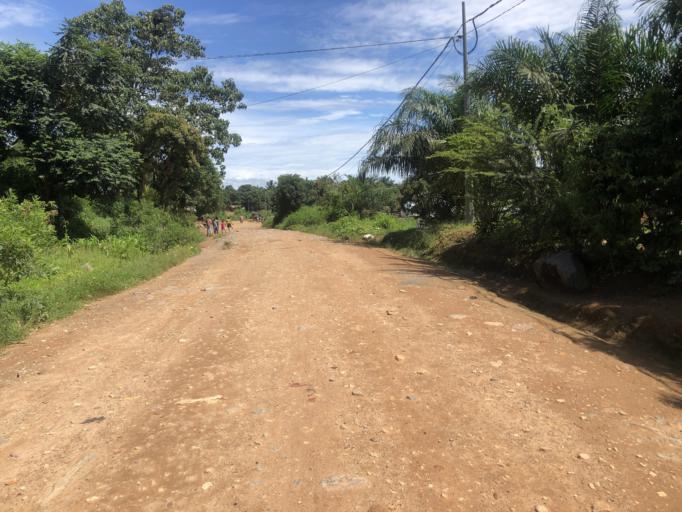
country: SL
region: Eastern Province
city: Koidu
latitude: 8.6422
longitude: -10.9546
